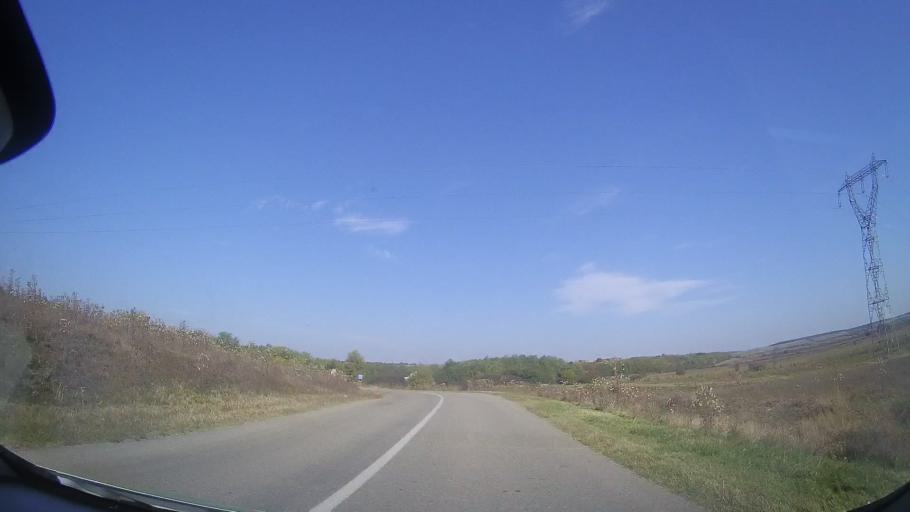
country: RO
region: Timis
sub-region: Comuna Ghizela
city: Ghizela
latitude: 45.8069
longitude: 21.7211
